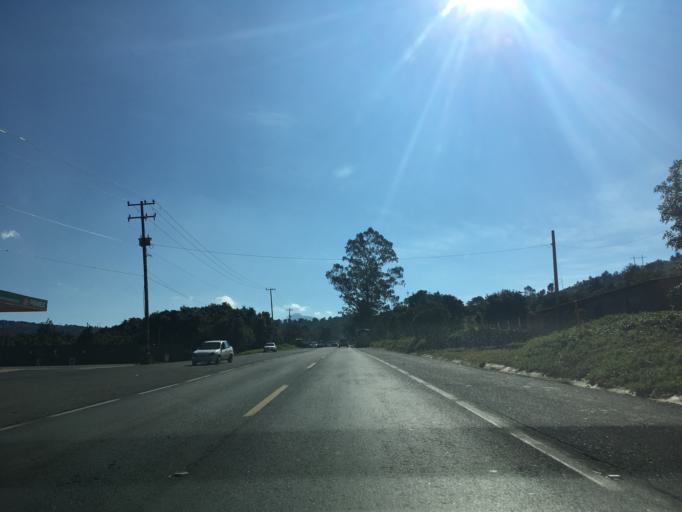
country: MX
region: Michoacan
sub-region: Chilchota
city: Tacuro (Santa Maria Tacuro)
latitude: 19.8533
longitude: -102.0410
